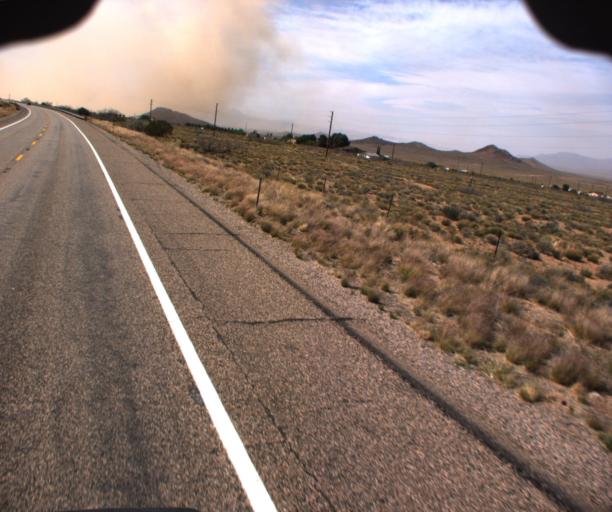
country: US
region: Arizona
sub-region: Mohave County
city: New Kingman-Butler
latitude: 35.4177
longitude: -113.7968
